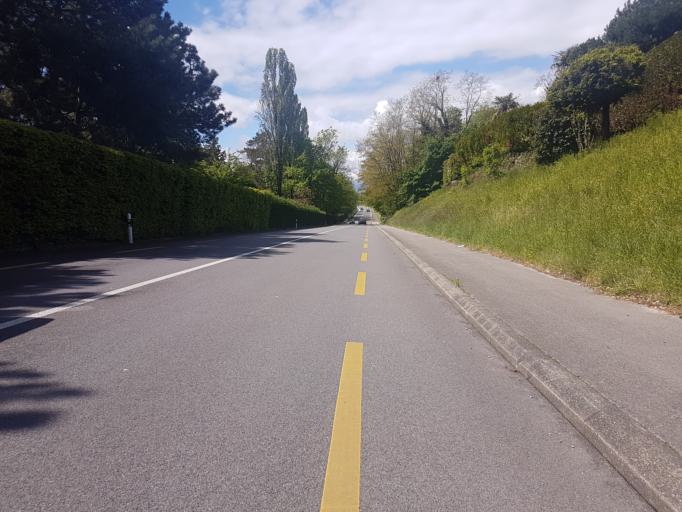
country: CH
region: Vaud
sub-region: Nyon District
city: Gland
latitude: 46.4275
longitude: 6.2975
